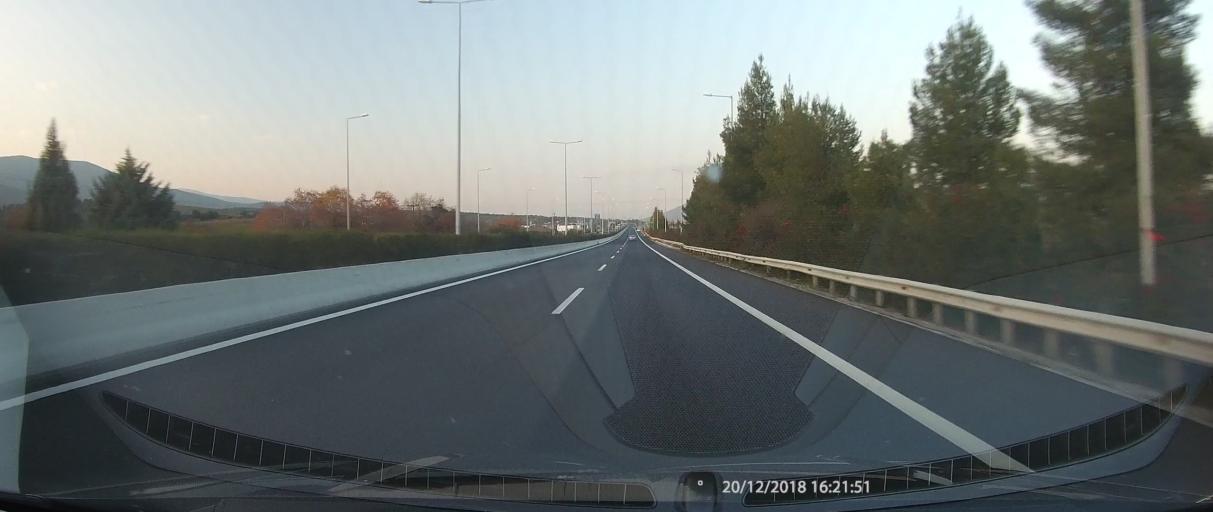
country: GR
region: Thessaly
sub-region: Nomos Magnisias
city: Sourpi
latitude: 39.0573
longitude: 22.8902
